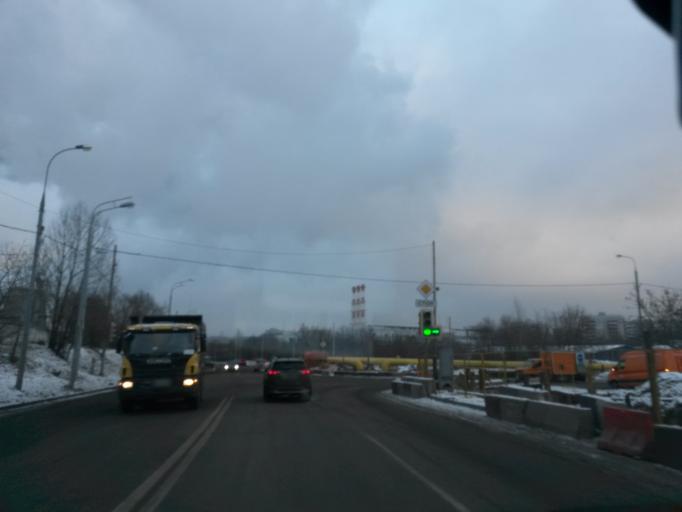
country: RU
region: Moscow
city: Ochakovo-Matveyevskoye
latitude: 55.6914
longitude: 37.4449
